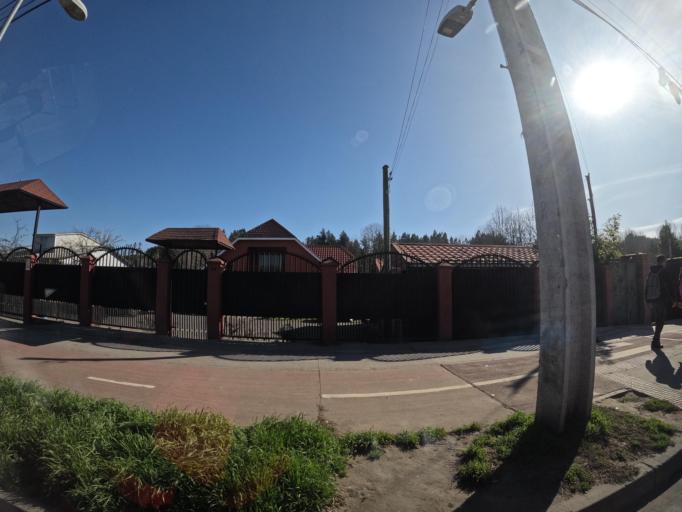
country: CL
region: Biobio
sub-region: Provincia de Concepcion
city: Chiguayante
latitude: -36.9666
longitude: -72.9365
